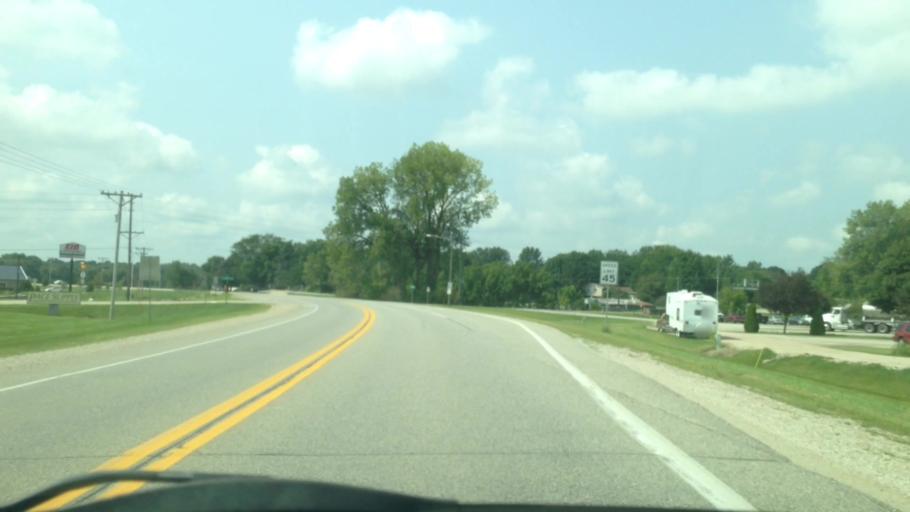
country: US
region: Iowa
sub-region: Linn County
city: Fairfax
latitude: 41.9283
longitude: -91.7811
